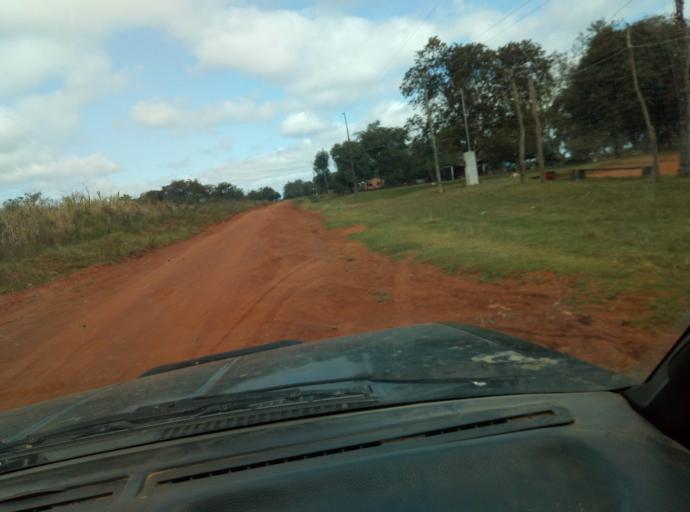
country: PY
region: Caaguazu
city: Doctor Cecilio Baez
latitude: -25.1510
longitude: -56.2909
